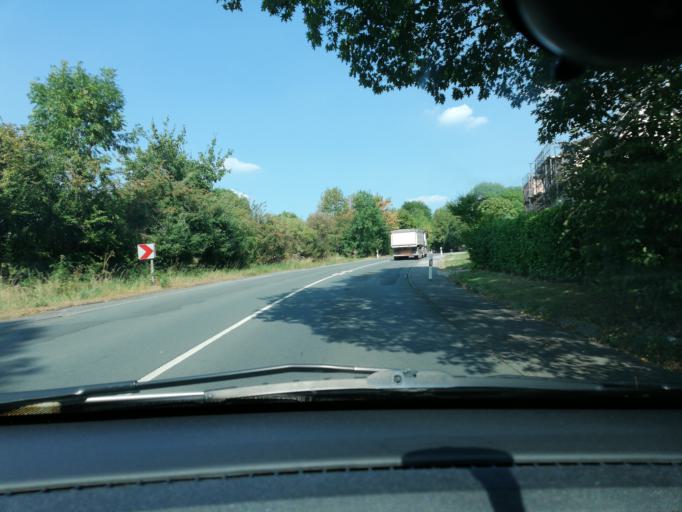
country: DE
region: North Rhine-Westphalia
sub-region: Regierungsbezirk Arnsberg
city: Schwelm
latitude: 51.3006
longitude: 7.3098
